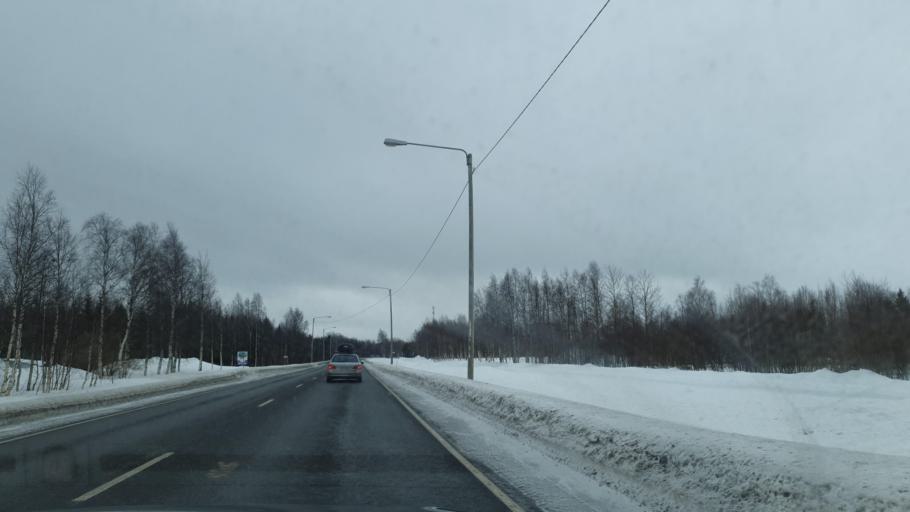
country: FI
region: Lapland
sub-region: Kemi-Tornio
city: Tornio
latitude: 65.8766
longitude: 24.1588
